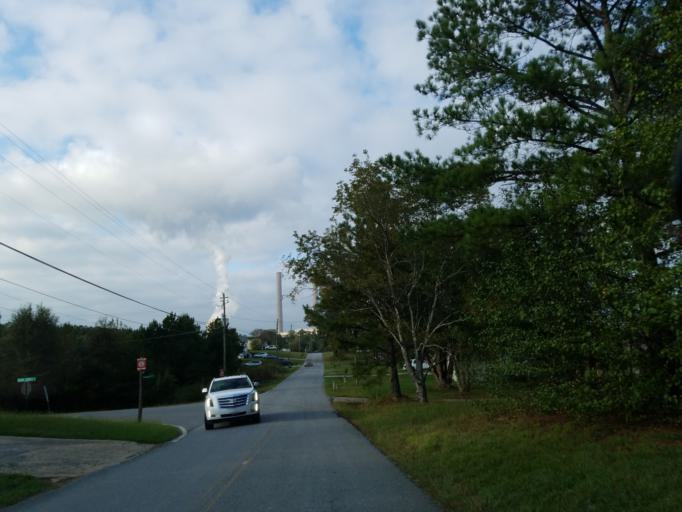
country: US
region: Georgia
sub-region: Bartow County
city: Euharlee
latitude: 34.1083
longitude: -84.9181
